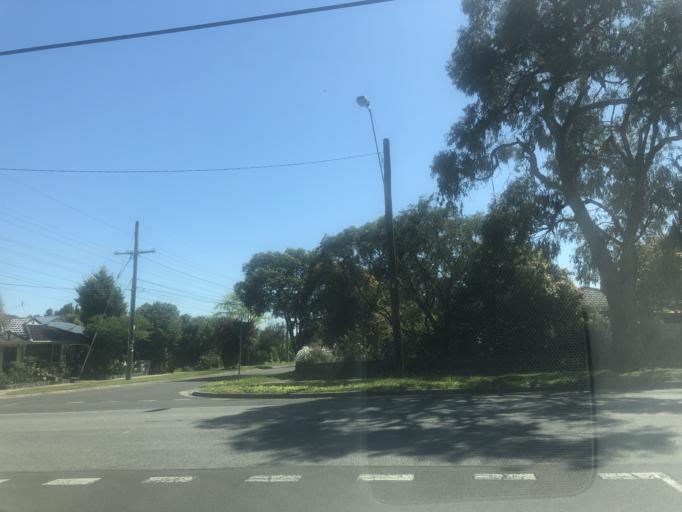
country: AU
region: Victoria
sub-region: Monash
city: Notting Hill
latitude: -37.8954
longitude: 145.1699
